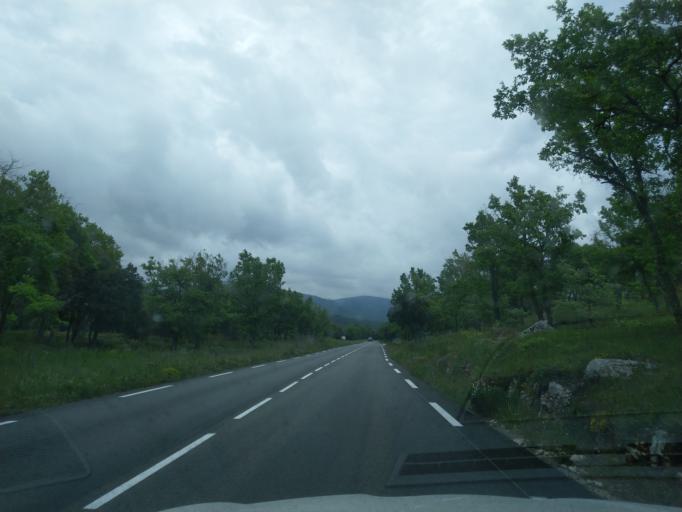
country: FR
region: Provence-Alpes-Cote d'Azur
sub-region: Departement du Var
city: Signes
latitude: 43.2801
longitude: 5.8209
